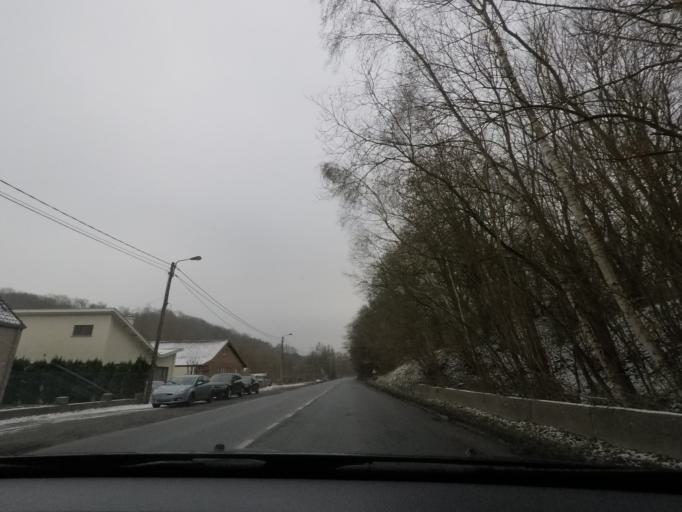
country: BE
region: Wallonia
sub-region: Province de Namur
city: Sombreffe
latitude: 50.4811
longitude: 4.6697
